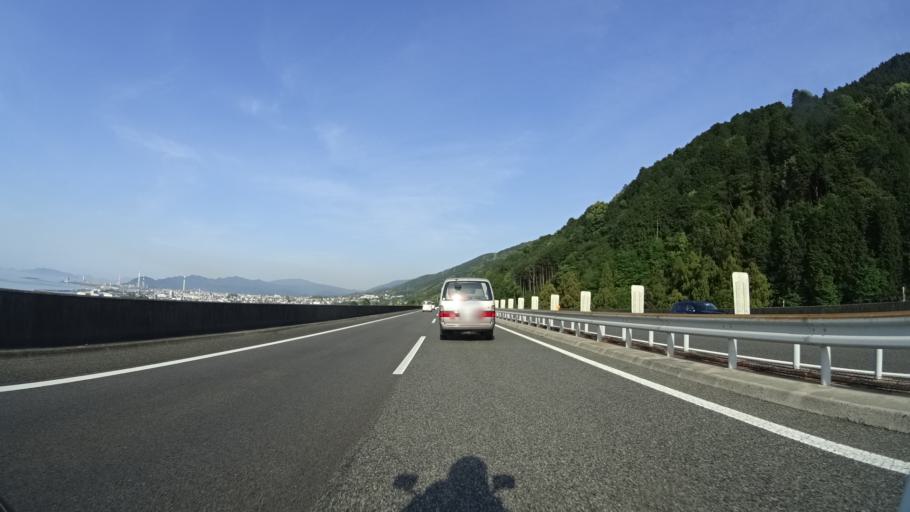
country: JP
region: Ehime
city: Kawanoecho
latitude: 33.9609
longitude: 133.5056
